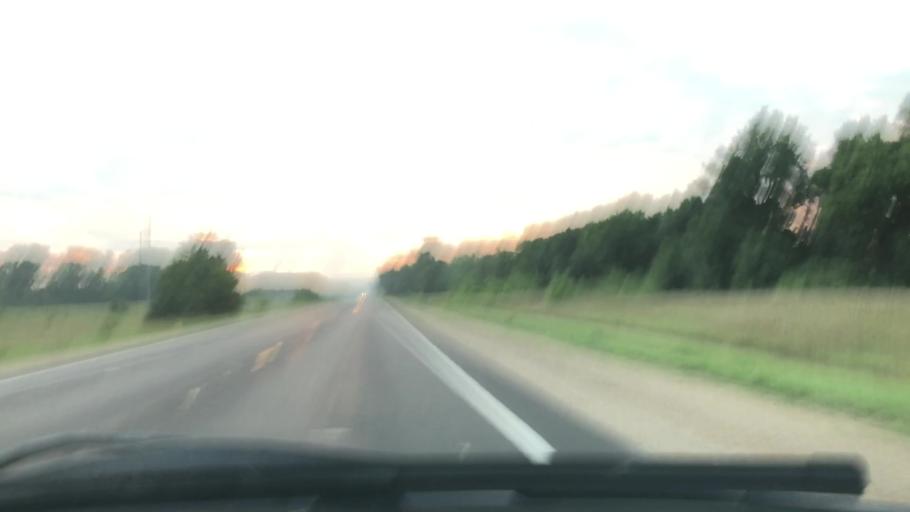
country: US
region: Wisconsin
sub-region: Sauk County
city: Spring Green
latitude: 43.1990
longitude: -90.2394
